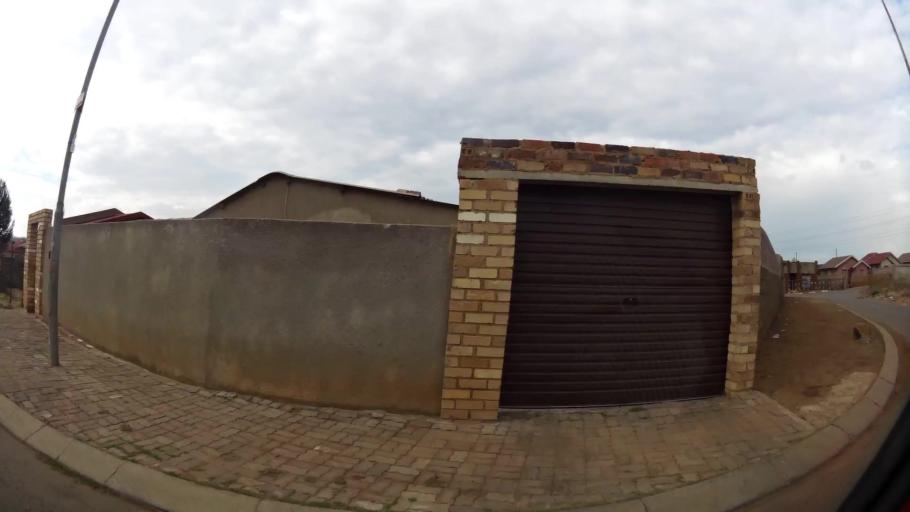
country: ZA
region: Gauteng
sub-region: City of Johannesburg Metropolitan Municipality
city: Soweto
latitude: -26.2421
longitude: 27.8592
